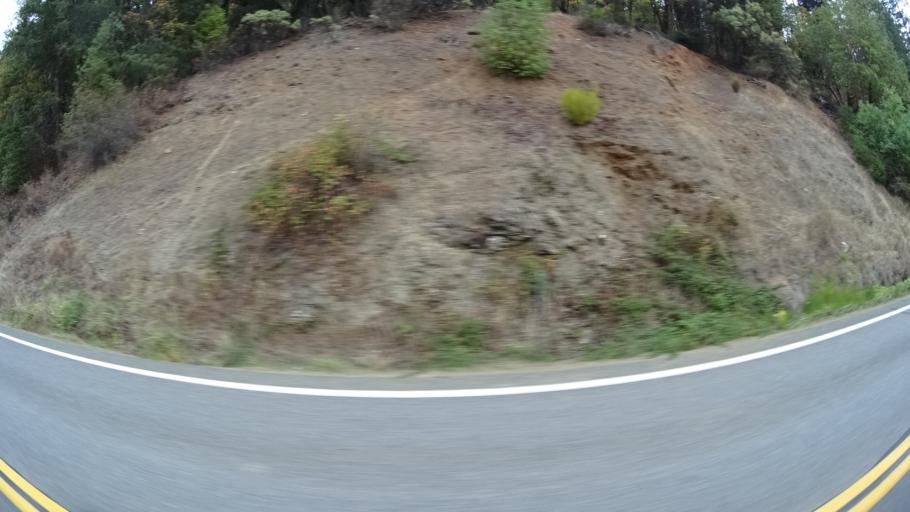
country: US
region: California
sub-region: Siskiyou County
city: Happy Camp
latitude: 41.8088
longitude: -123.3500
